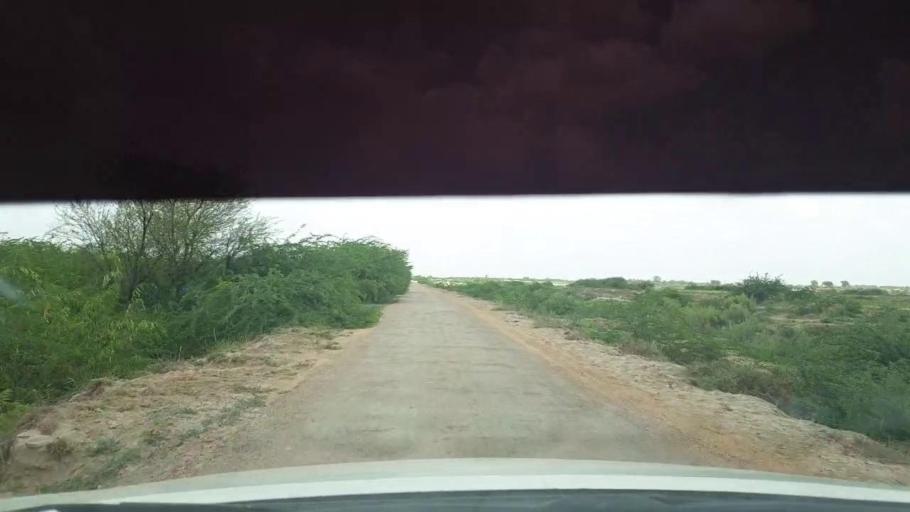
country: PK
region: Sindh
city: Kadhan
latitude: 24.4801
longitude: 69.0661
